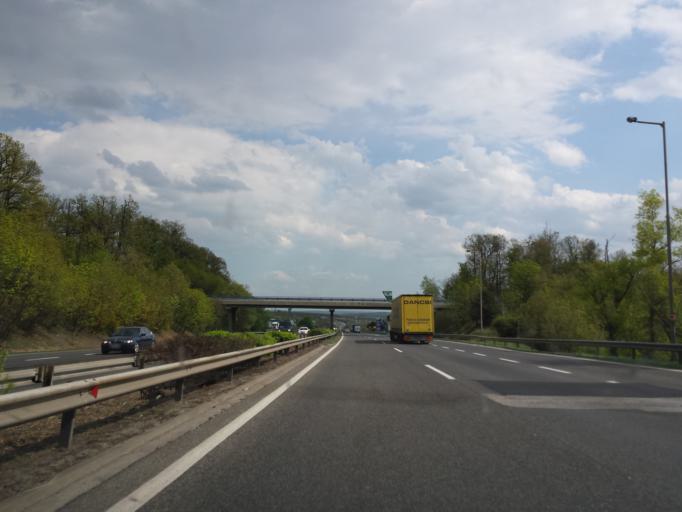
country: HU
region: Fejer
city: Szarliget
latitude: 47.5050
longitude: 18.5455
